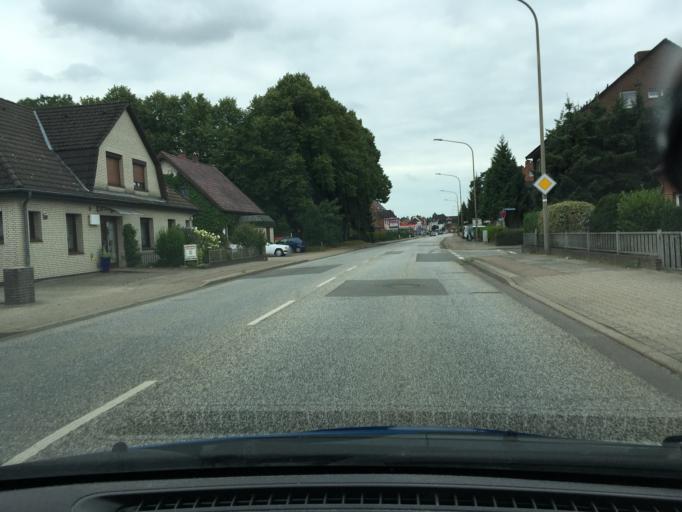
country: DE
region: Schleswig-Holstein
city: Geesthacht
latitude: 53.4466
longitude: 10.3616
